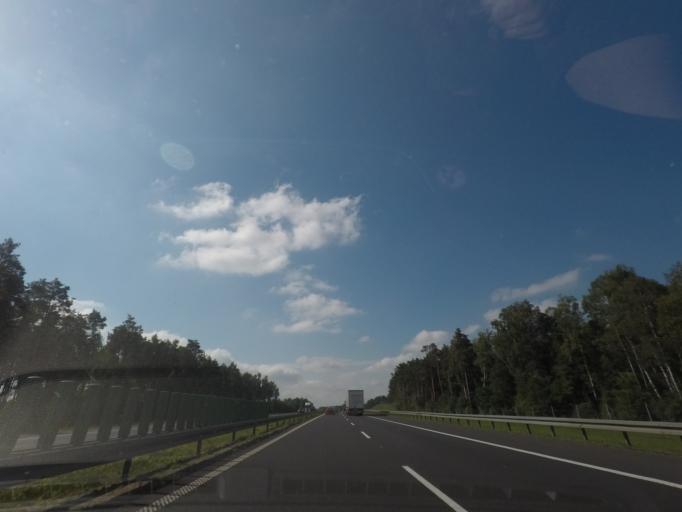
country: PL
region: Kujawsko-Pomorskie
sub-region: Powiat swiecki
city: Warlubie
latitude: 53.6659
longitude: 18.6393
